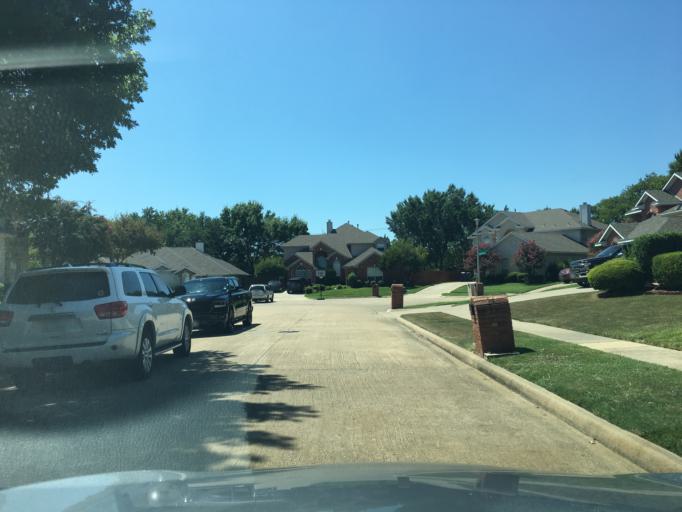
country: US
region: Texas
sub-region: Dallas County
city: Sachse
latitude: 32.9632
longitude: -96.6336
